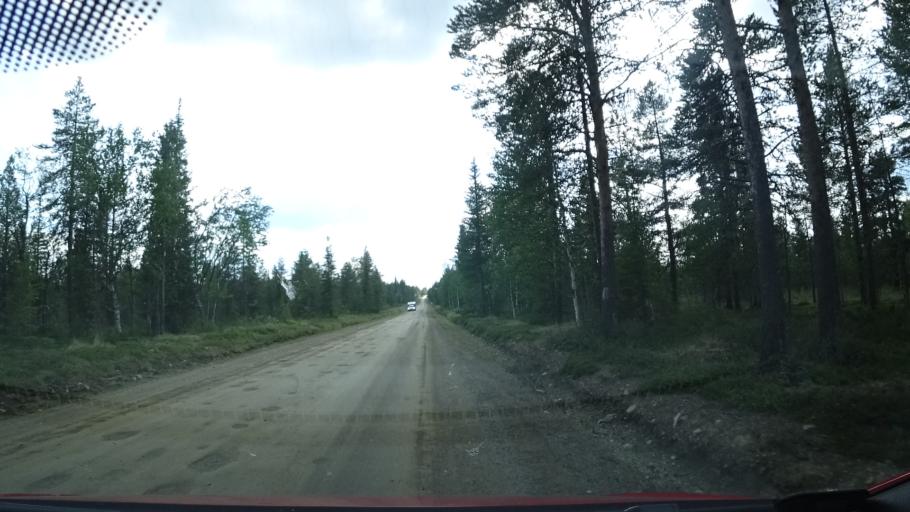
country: FI
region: Lapland
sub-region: Tunturi-Lappi
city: Kittilae
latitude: 68.0851
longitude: 25.4245
